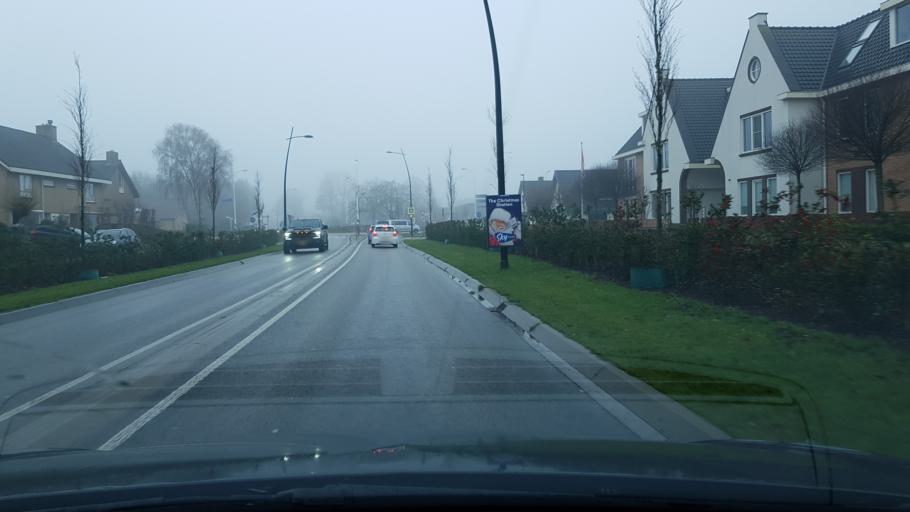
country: NL
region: Gelderland
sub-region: Gemeente Putten
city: Putten
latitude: 52.2516
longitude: 5.6071
